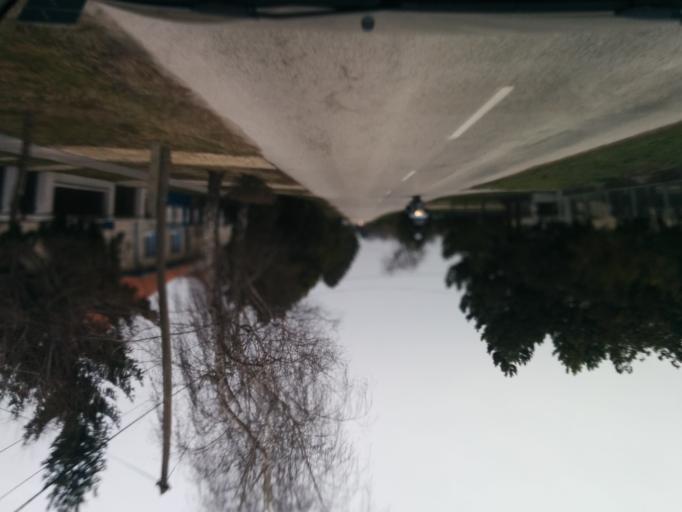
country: SK
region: Trnavsky
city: Sladkovicovo
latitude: 48.2409
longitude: 17.6243
